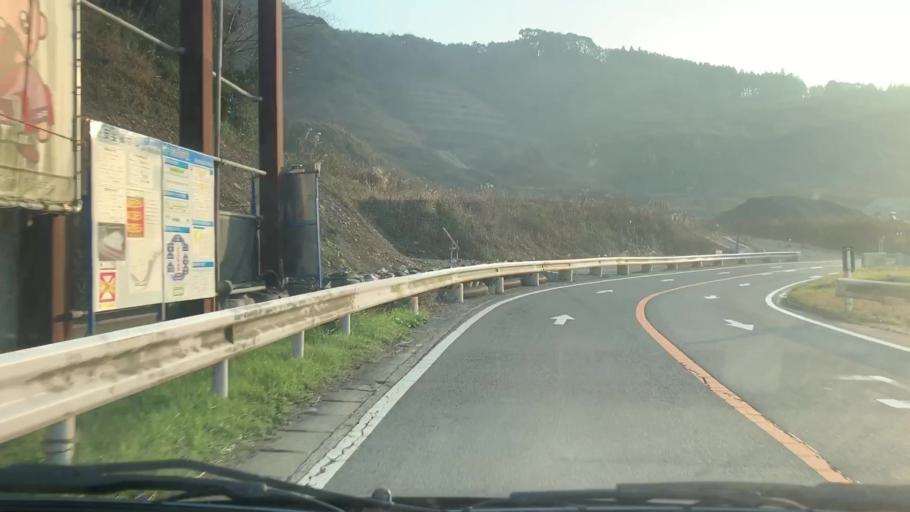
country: JP
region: Saga Prefecture
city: Takeocho-takeo
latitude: 33.2713
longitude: 130.1121
